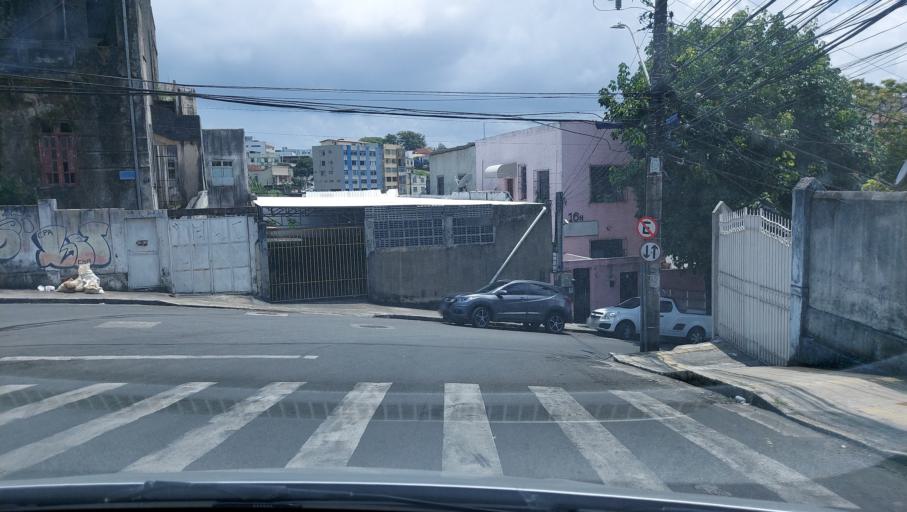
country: BR
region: Bahia
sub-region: Salvador
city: Salvador
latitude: -12.9705
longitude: -38.5005
